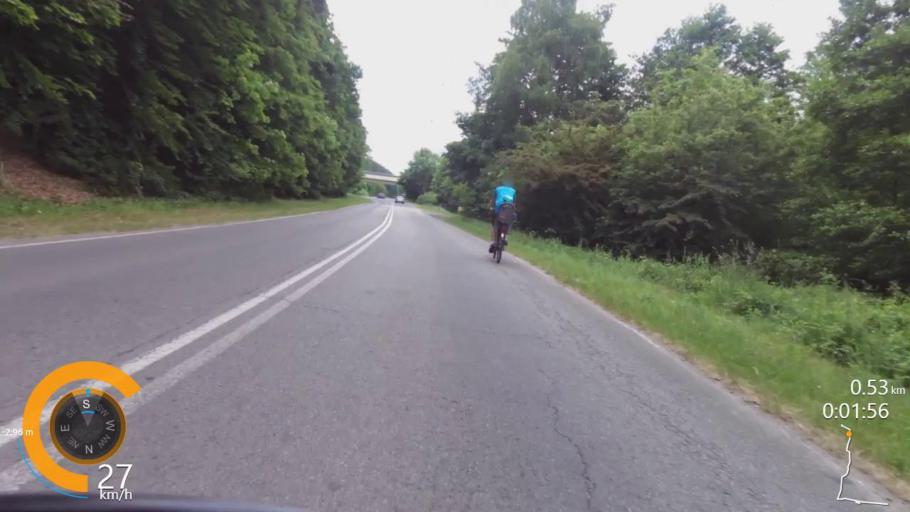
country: PL
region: West Pomeranian Voivodeship
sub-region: Powiat kamienski
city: Miedzyzdroje
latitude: 53.9087
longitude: 14.4375
